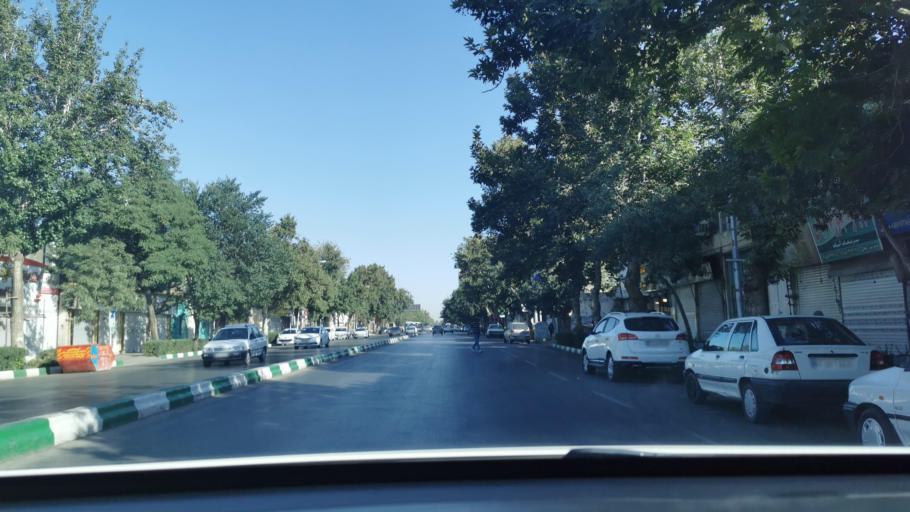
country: IR
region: Razavi Khorasan
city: Mashhad
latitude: 36.3085
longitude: 59.5947
